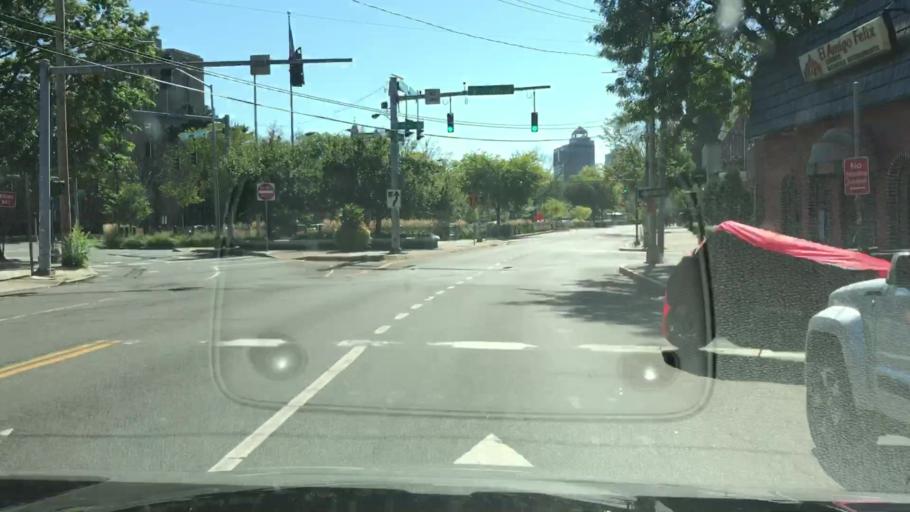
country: US
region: Connecticut
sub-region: New Haven County
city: New Haven
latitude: 41.3129
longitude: -72.9332
